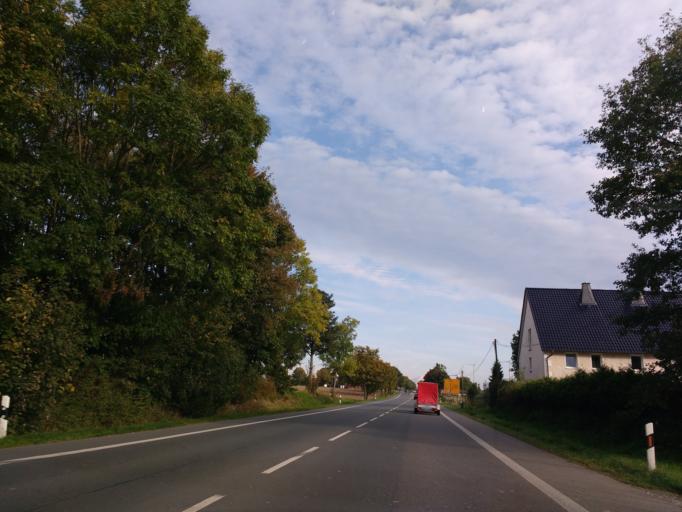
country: DE
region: North Rhine-Westphalia
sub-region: Regierungsbezirk Detmold
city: Paderborn
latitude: 51.6790
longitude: 8.8272
